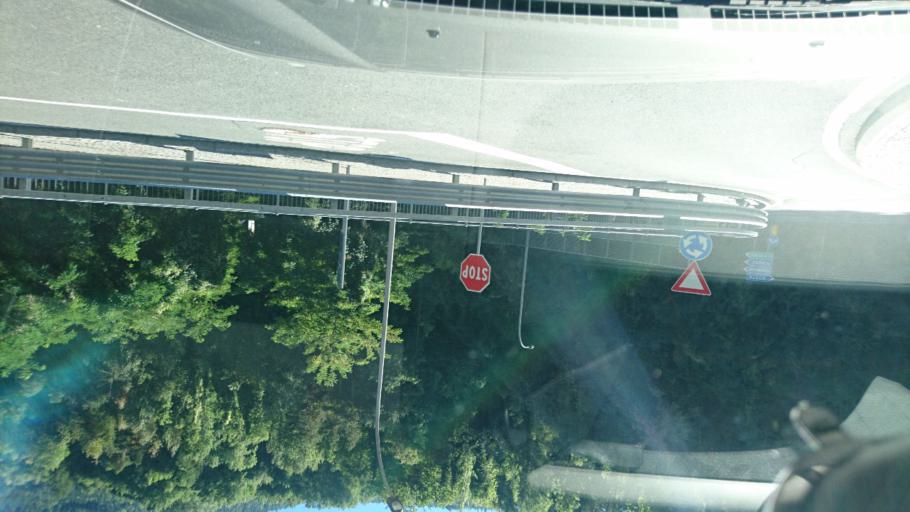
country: IT
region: Aosta Valley
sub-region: Valle d'Aosta
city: Avise
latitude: 45.7065
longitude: 7.1355
